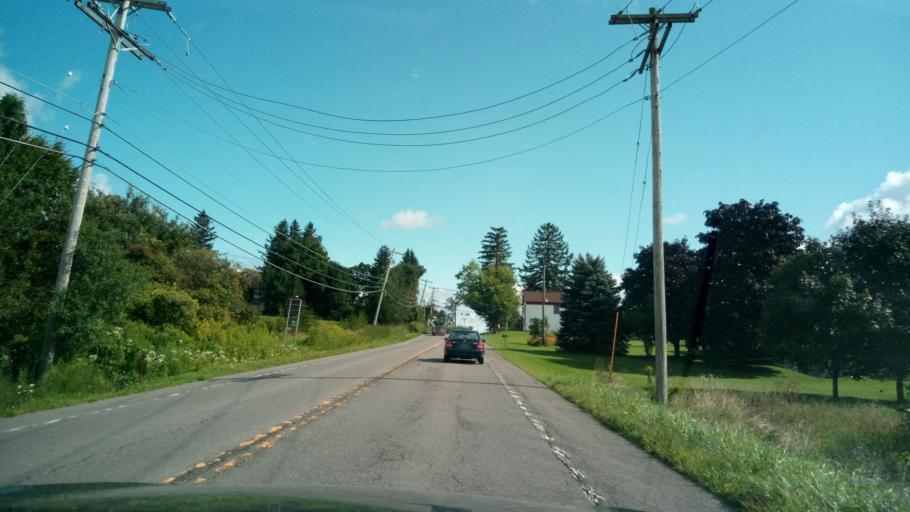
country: US
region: New York
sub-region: Onondaga County
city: Nedrow
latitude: 42.8095
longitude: -76.0835
